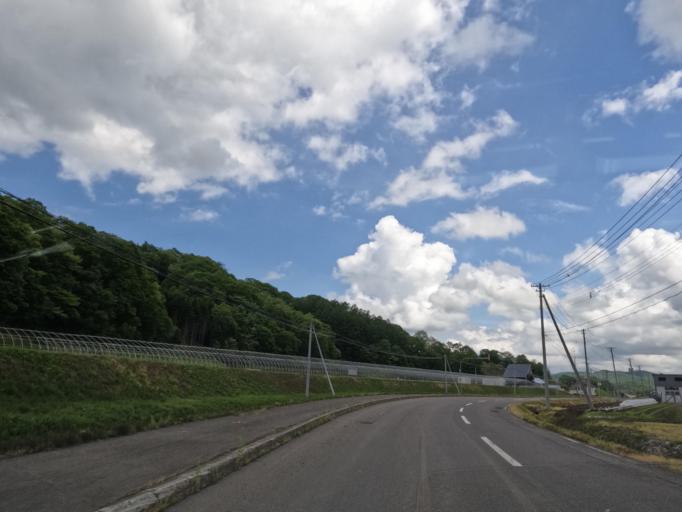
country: JP
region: Hokkaido
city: Takikawa
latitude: 43.5951
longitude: 141.7454
